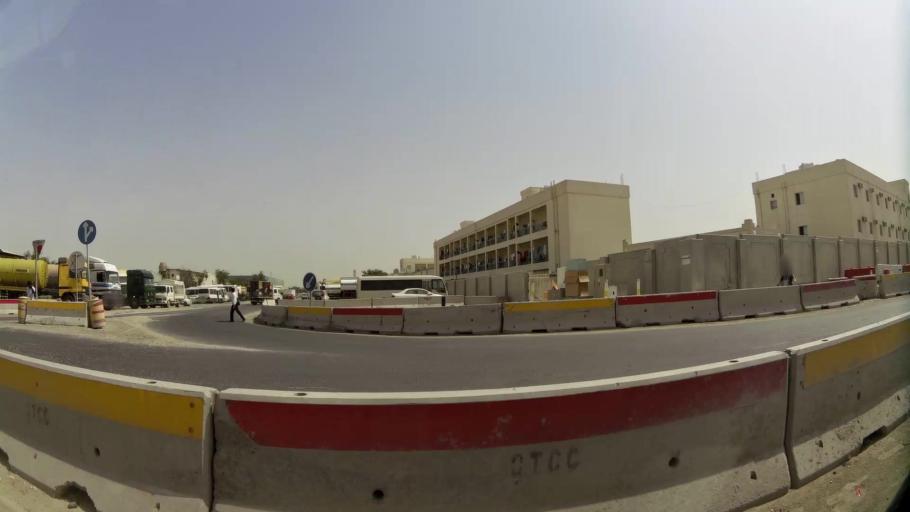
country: QA
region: Baladiyat ar Rayyan
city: Ar Rayyan
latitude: 25.1938
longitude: 51.4180
